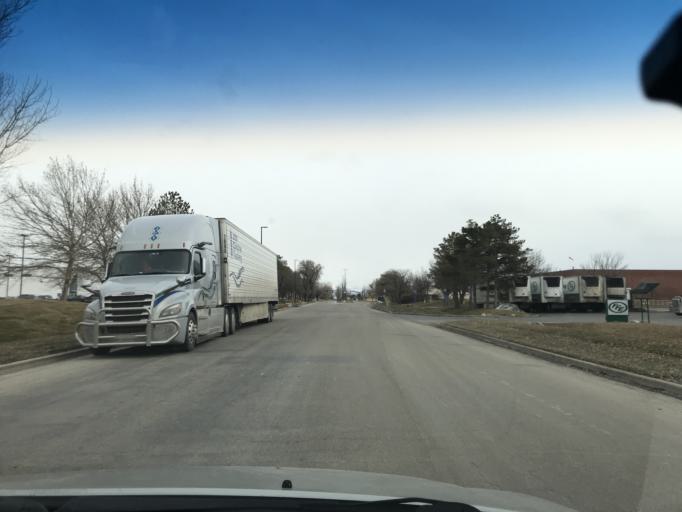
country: US
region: Utah
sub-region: Salt Lake County
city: West Valley City
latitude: 40.7813
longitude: -112.0296
